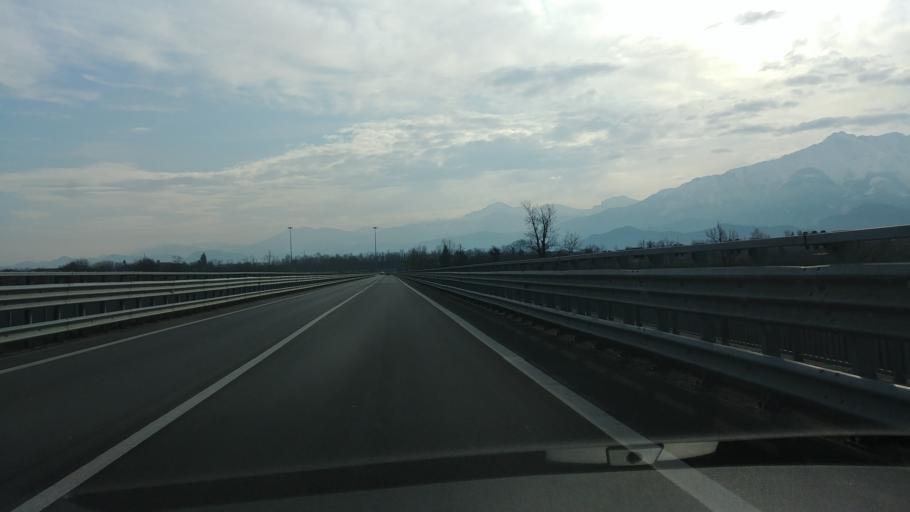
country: IT
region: Piedmont
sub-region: Provincia di Cuneo
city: Cuneo
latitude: 44.3709
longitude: 7.5467
